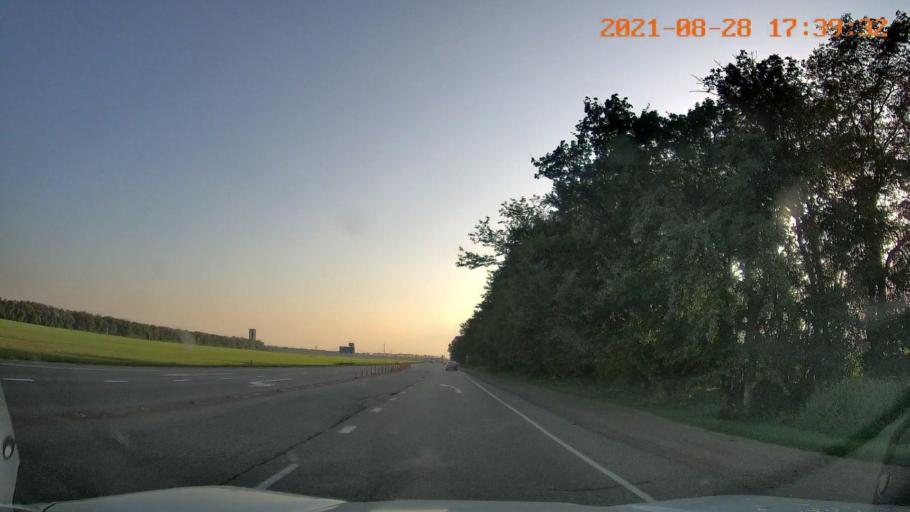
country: RU
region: Krasnodarskiy
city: Novokubansk
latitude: 45.0562
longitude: 40.9819
